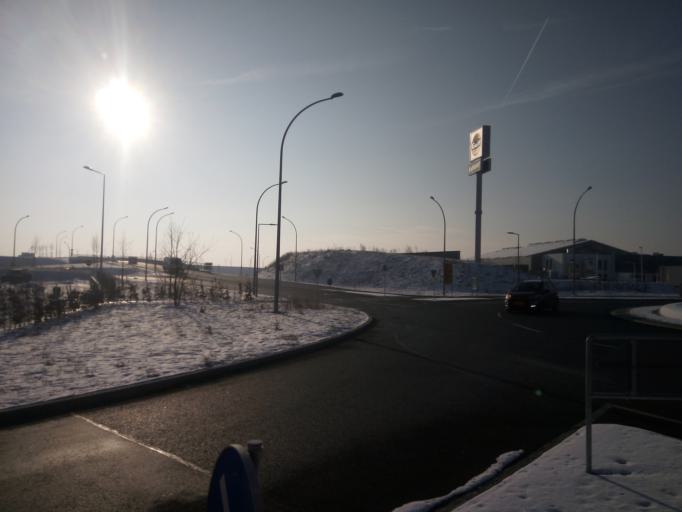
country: LU
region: Grevenmacher
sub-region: Canton de Grevenmacher
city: Junglinster
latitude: 49.7186
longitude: 6.2690
